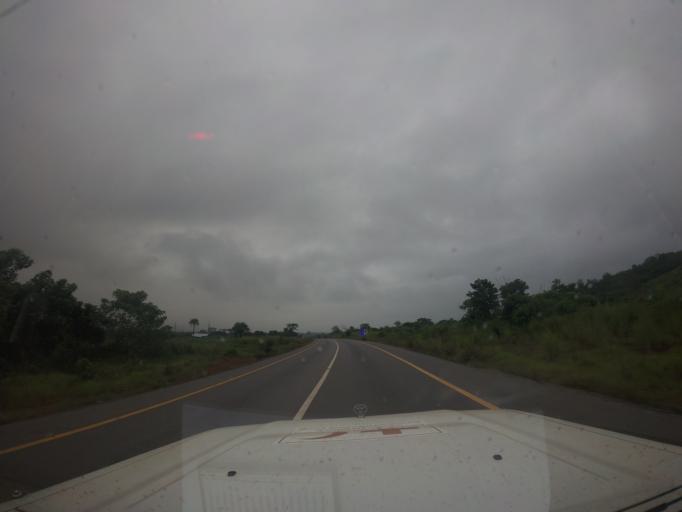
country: SL
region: Eastern Province
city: Hangha
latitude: 7.9248
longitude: -11.1511
